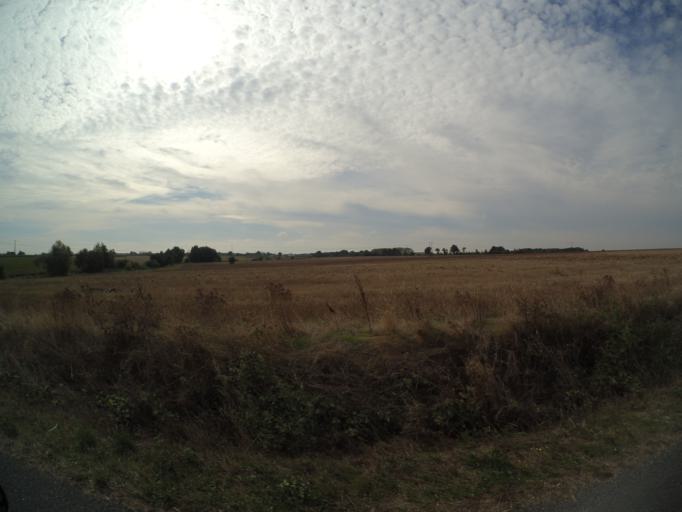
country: FR
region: Pays de la Loire
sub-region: Departement de Maine-et-Loire
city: Martigne-Briand
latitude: 47.2086
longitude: -0.4816
